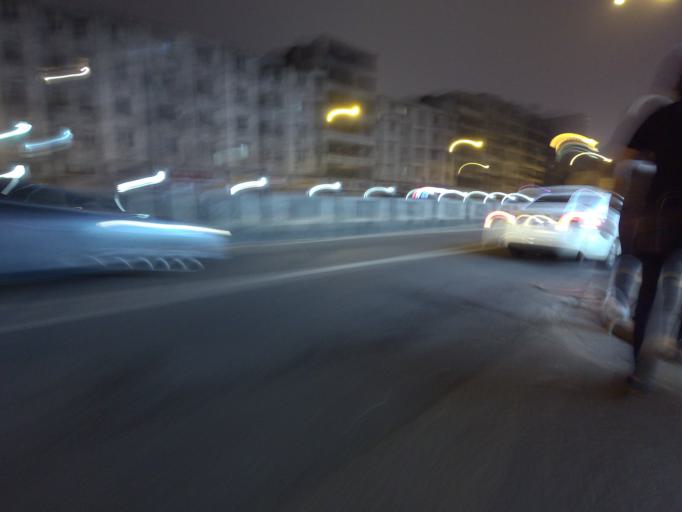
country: CN
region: Sichuan
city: Chengdu
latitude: 30.6682
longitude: 104.0581
